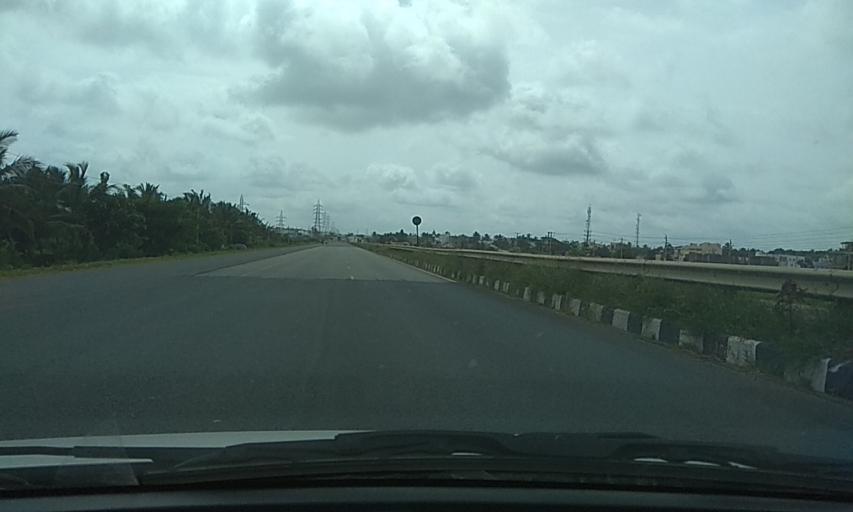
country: IN
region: Karnataka
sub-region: Davanagere
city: Harihar
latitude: 14.4444
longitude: 75.8922
